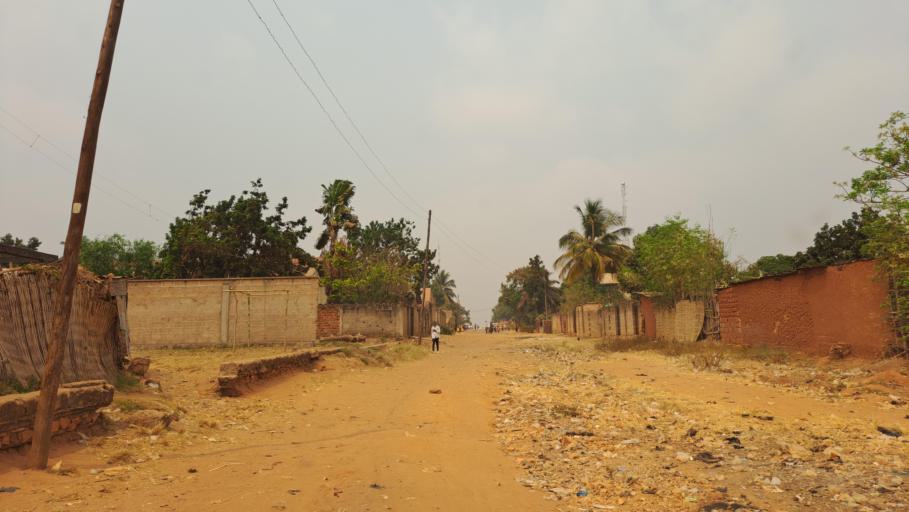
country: CD
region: Kasai-Oriental
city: Mbuji-Mayi
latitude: -6.1075
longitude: 23.5960
